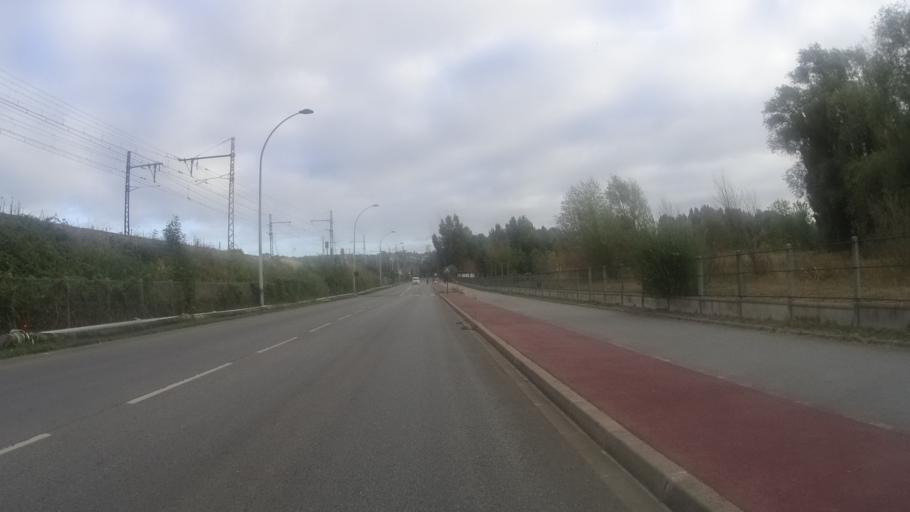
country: FR
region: Ile-de-France
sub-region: Departement de l'Essonne
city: Villabe
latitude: 48.5991
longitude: 2.4597
